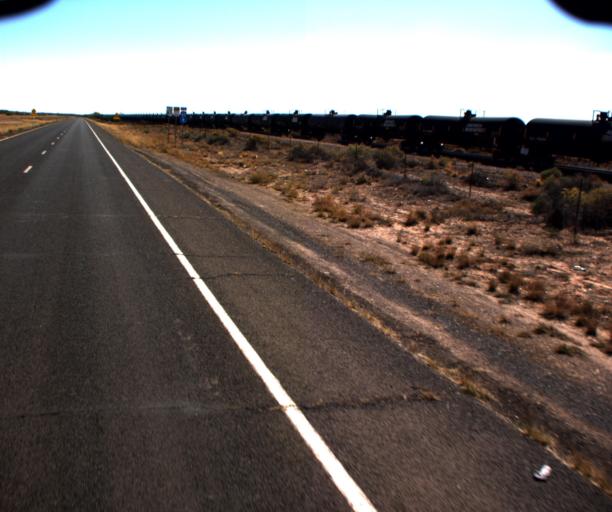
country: US
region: Arizona
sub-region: Navajo County
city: Winslow
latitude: 35.0118
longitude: -110.6713
